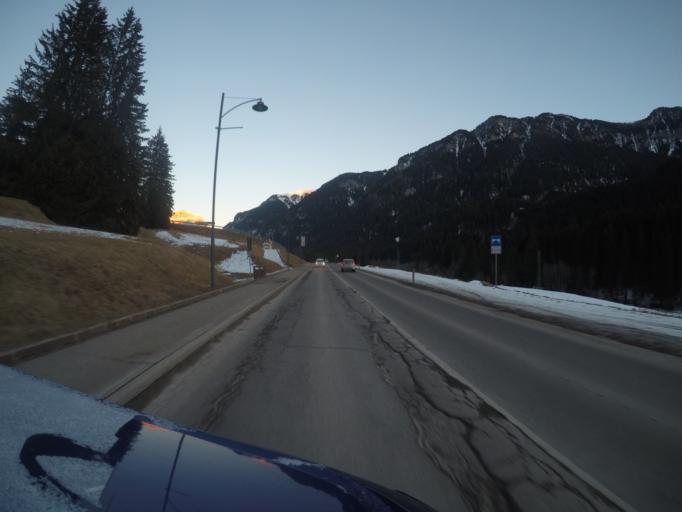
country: IT
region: Trentino-Alto Adige
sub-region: Provincia di Trento
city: Mazzin
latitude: 46.4602
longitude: 11.7024
